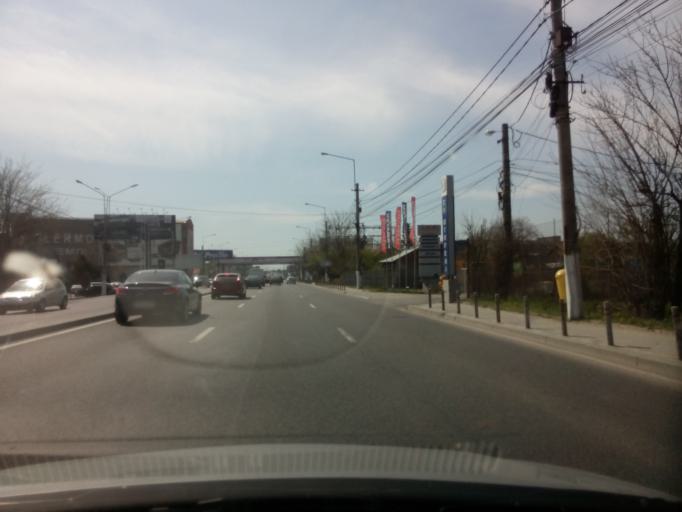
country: RO
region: Ilfov
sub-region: Comuna Otopeni
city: Otopeni
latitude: 44.5430
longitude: 26.0686
